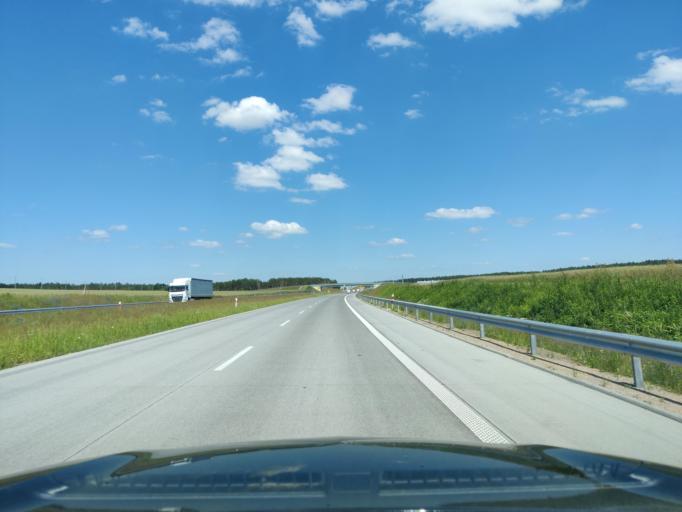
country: PL
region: Masovian Voivodeship
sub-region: Powiat mlawski
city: Strzegowo
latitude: 52.9708
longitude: 20.3218
